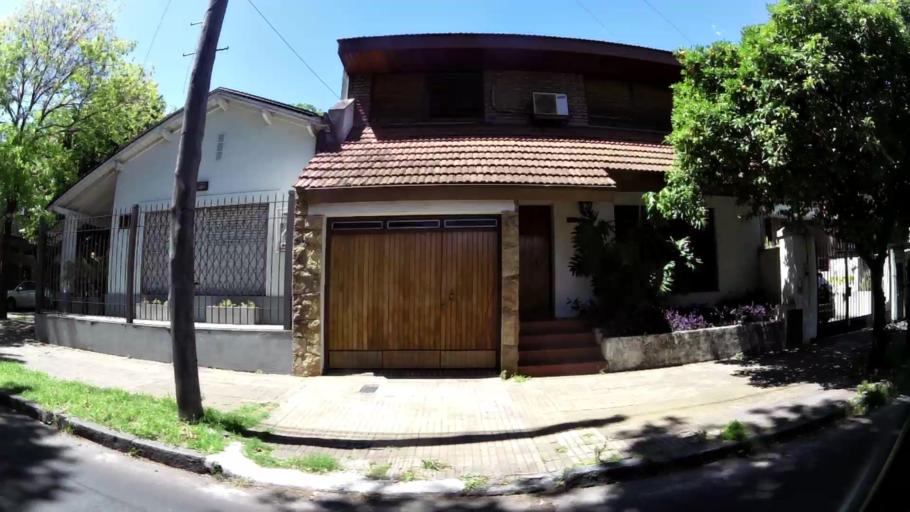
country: AR
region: Buenos Aires
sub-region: Partido de Vicente Lopez
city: Olivos
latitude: -34.5097
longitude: -58.4953
